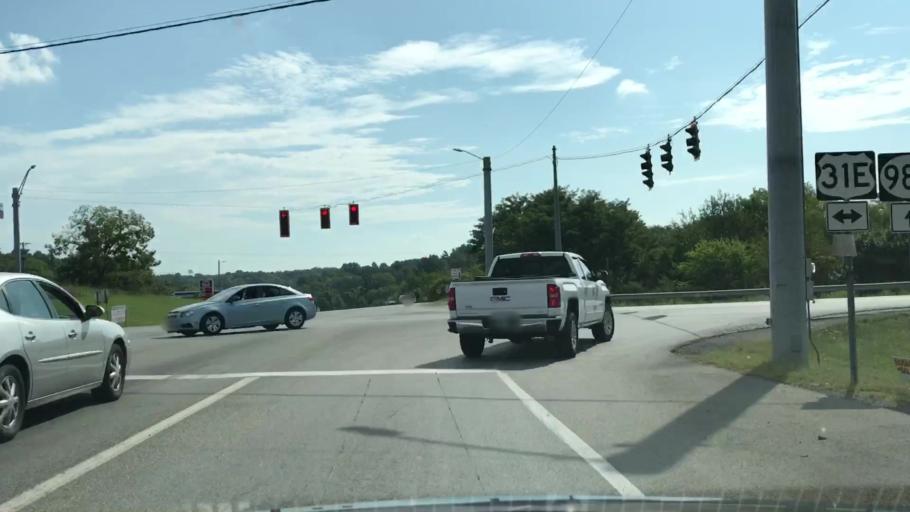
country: US
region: Kentucky
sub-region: Allen County
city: Scottsville
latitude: 36.7562
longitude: -86.2138
